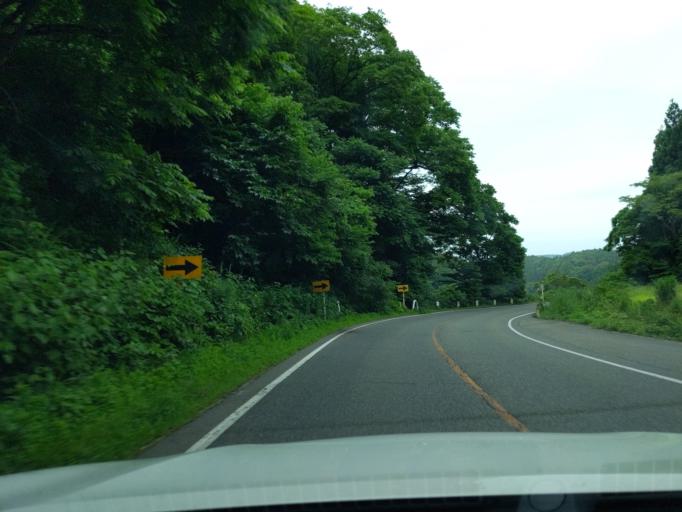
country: JP
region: Niigata
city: Nagaoka
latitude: 37.4435
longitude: 138.7014
